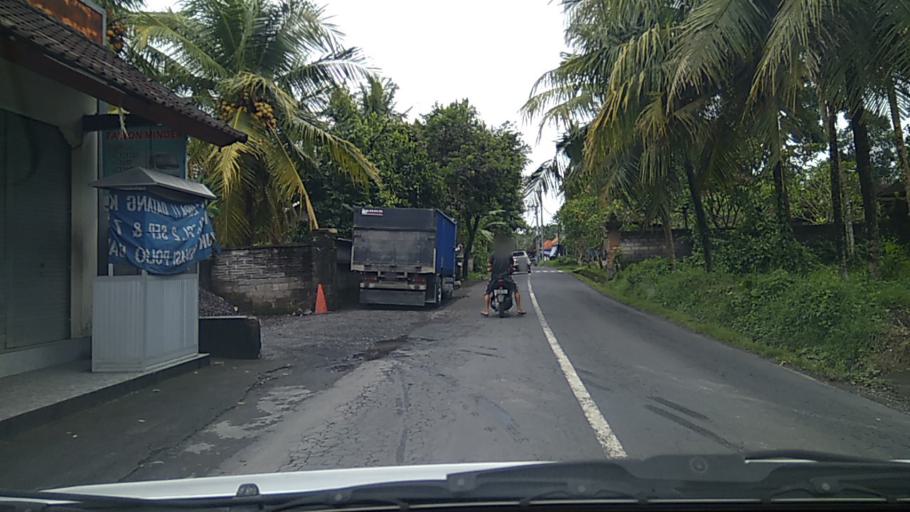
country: ID
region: Bali
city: Banjar Tebongkang
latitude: -8.5234
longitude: 115.2388
